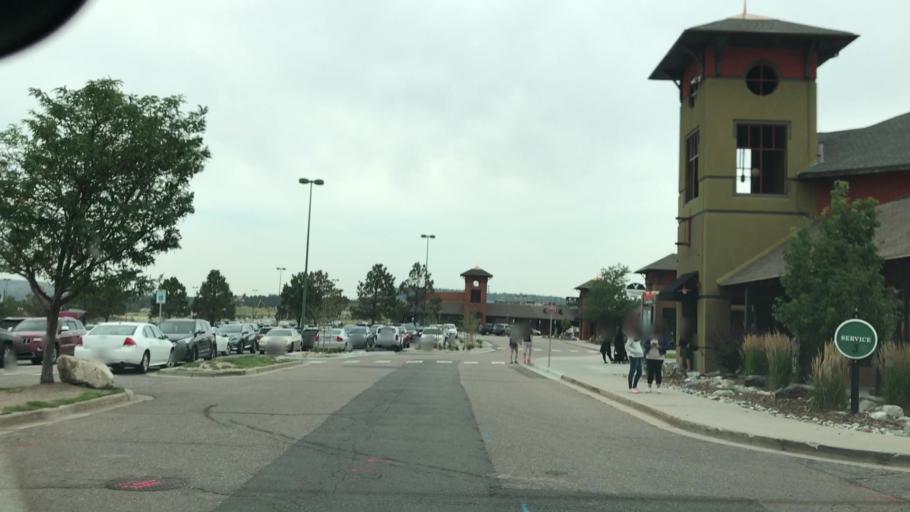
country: US
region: Colorado
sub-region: Douglas County
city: Castle Rock
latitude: 39.4148
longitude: -104.8739
